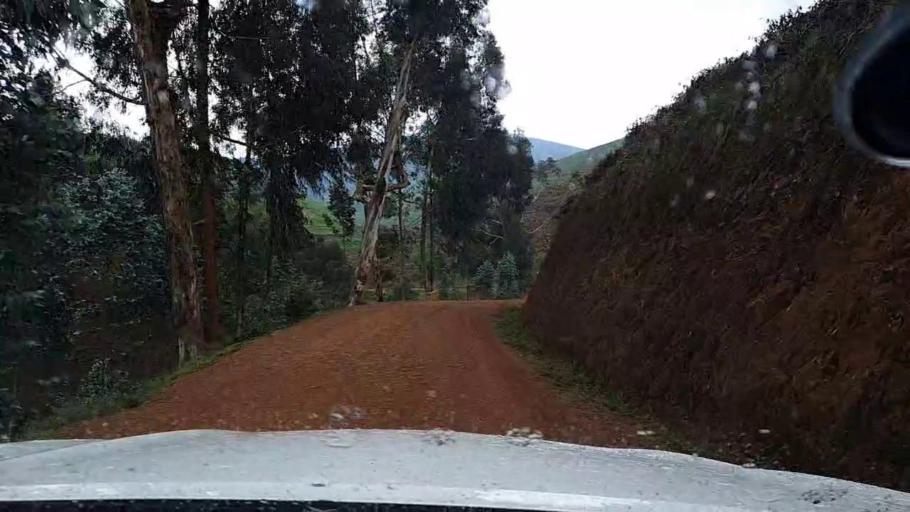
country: RW
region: Western Province
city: Kibuye
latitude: -2.1619
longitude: 29.4345
